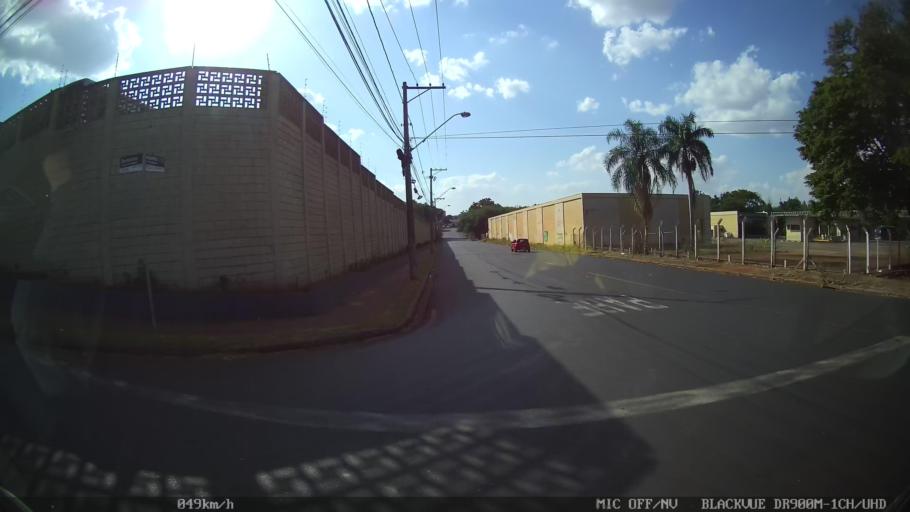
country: BR
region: Sao Paulo
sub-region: Ribeirao Preto
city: Ribeirao Preto
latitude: -21.1781
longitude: -47.8332
